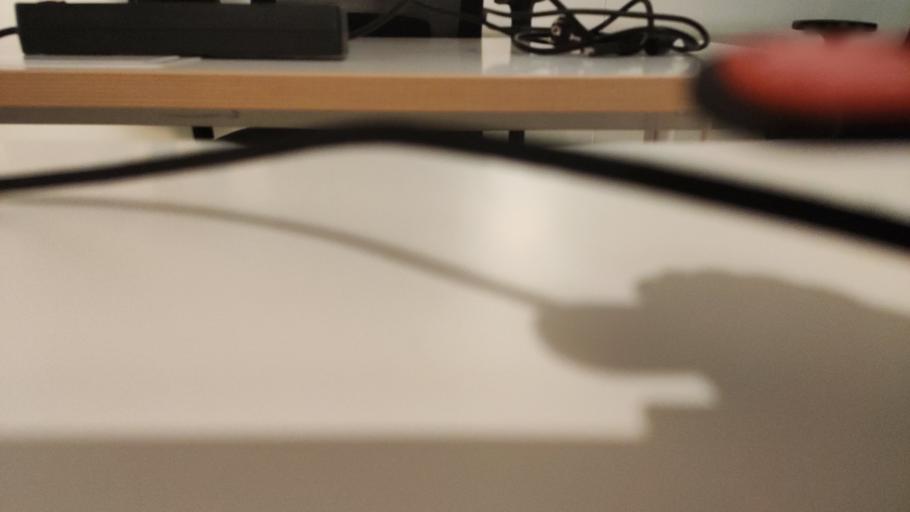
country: RU
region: Moskovskaya
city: Proletarskiy
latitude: 54.9832
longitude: 37.3311
